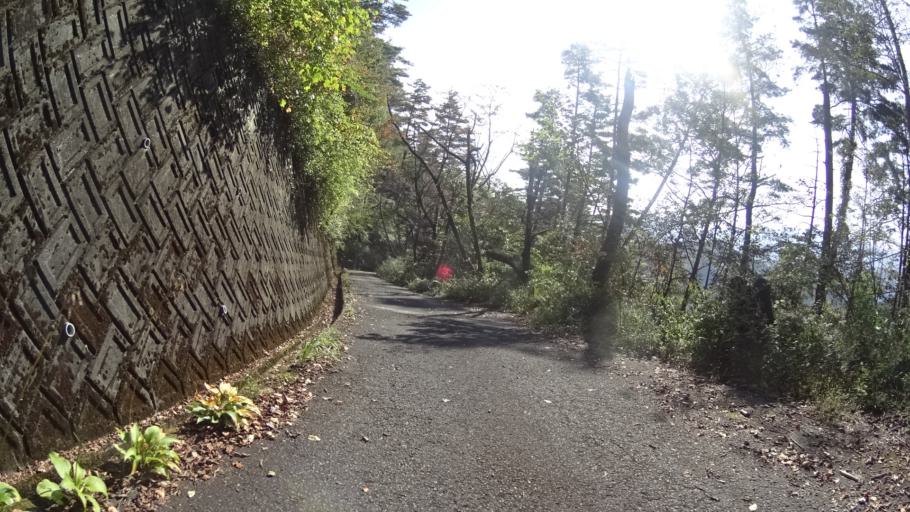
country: JP
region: Yamanashi
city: Otsuki
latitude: 35.5770
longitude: 138.9853
